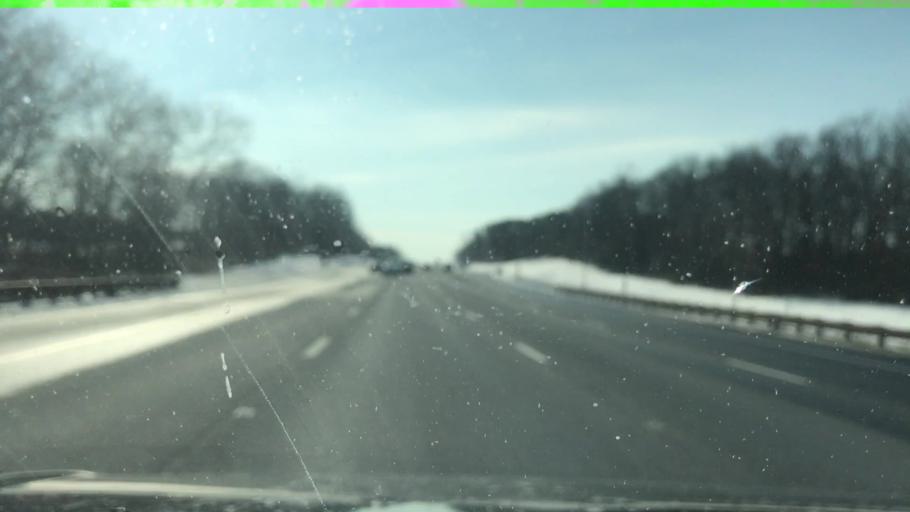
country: US
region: New Jersey
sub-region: Monmouth County
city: Ramtown
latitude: 40.1588
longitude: -74.1037
